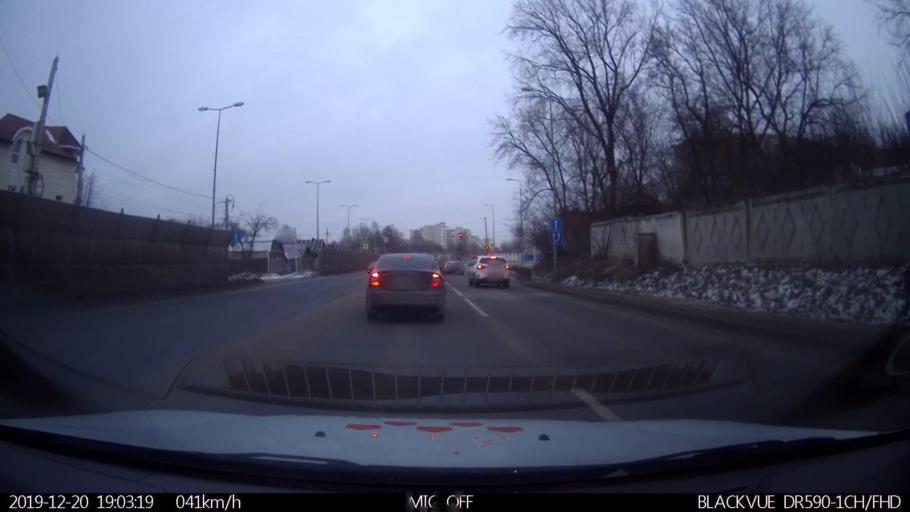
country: RU
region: Nizjnij Novgorod
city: Nizhniy Novgorod
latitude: 56.3085
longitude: 43.9757
